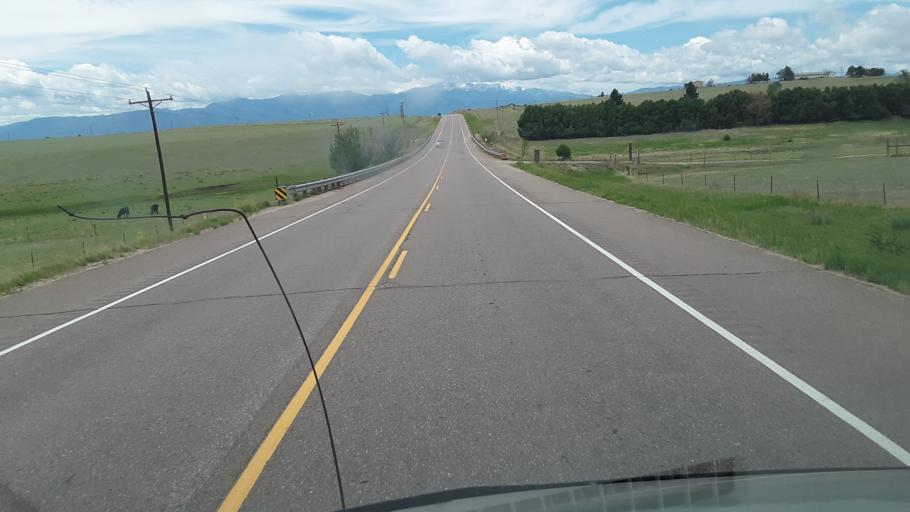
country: US
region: Colorado
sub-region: El Paso County
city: Cimarron Hills
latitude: 38.8387
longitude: -104.5635
